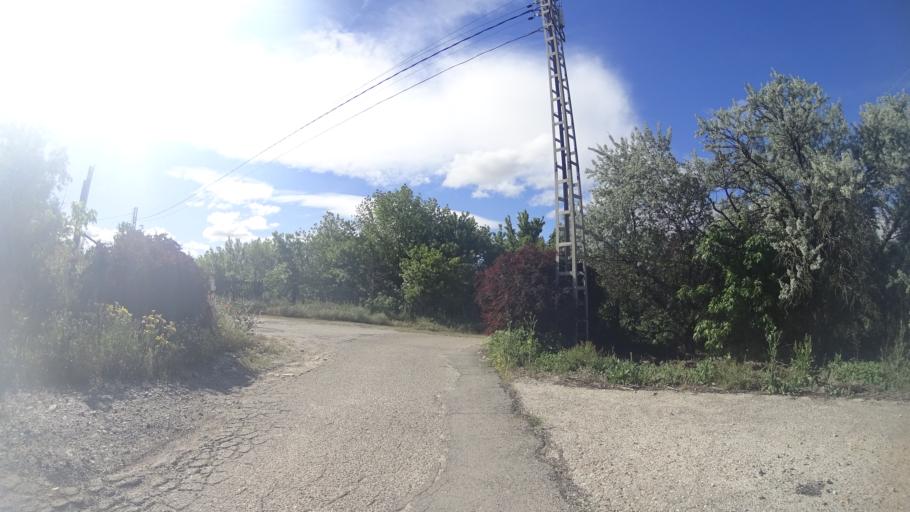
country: ES
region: Madrid
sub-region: Provincia de Madrid
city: Villanueva del Pardillo
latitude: 40.4953
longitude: -3.9406
